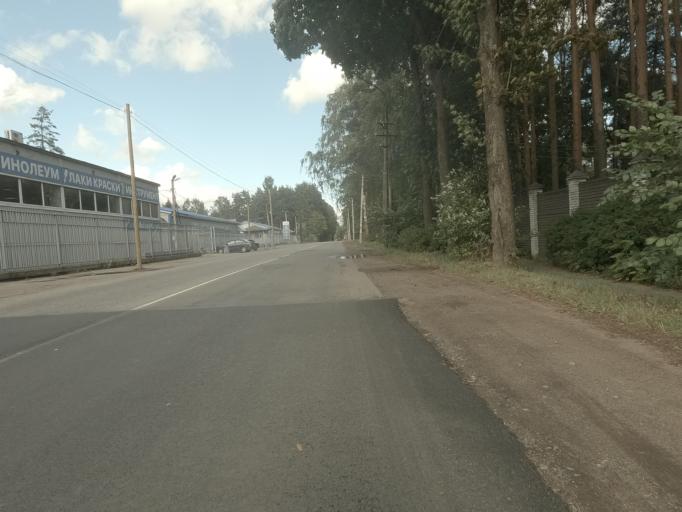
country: RU
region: Leningrad
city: Vsevolozhsk
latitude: 60.0145
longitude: 30.6681
